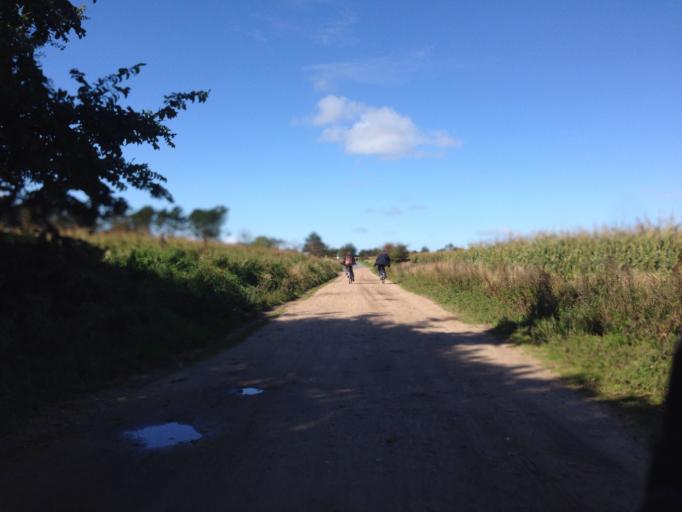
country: DE
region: Schleswig-Holstein
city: Nieblum
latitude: 54.6839
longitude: 8.4771
